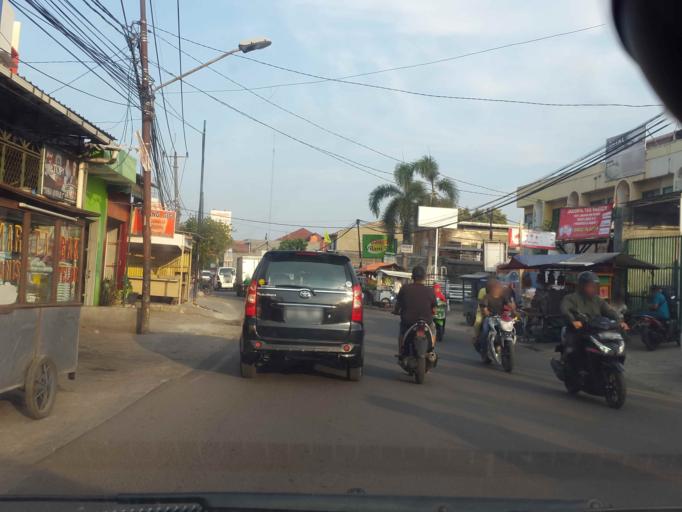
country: ID
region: Banten
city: South Tangerang
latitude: -6.2629
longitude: 106.7354
